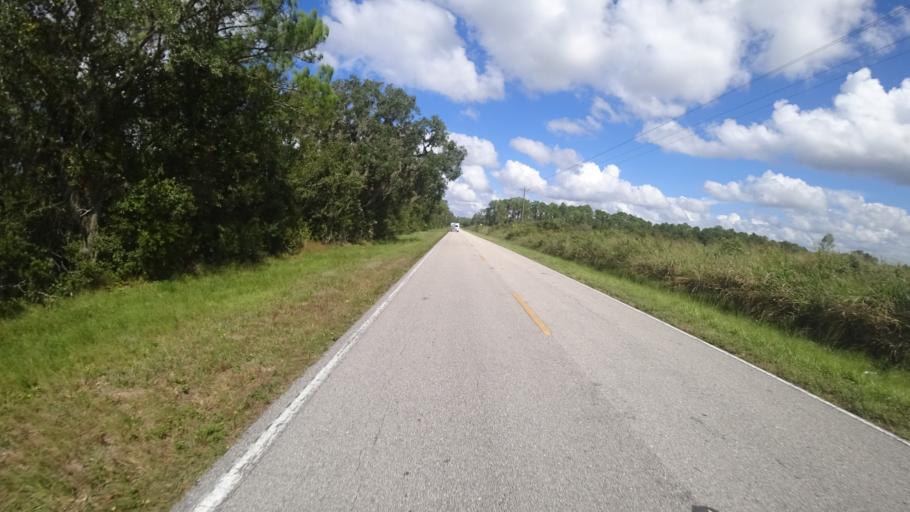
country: US
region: Florida
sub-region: Sarasota County
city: Lake Sarasota
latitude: 27.3797
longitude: -82.1398
